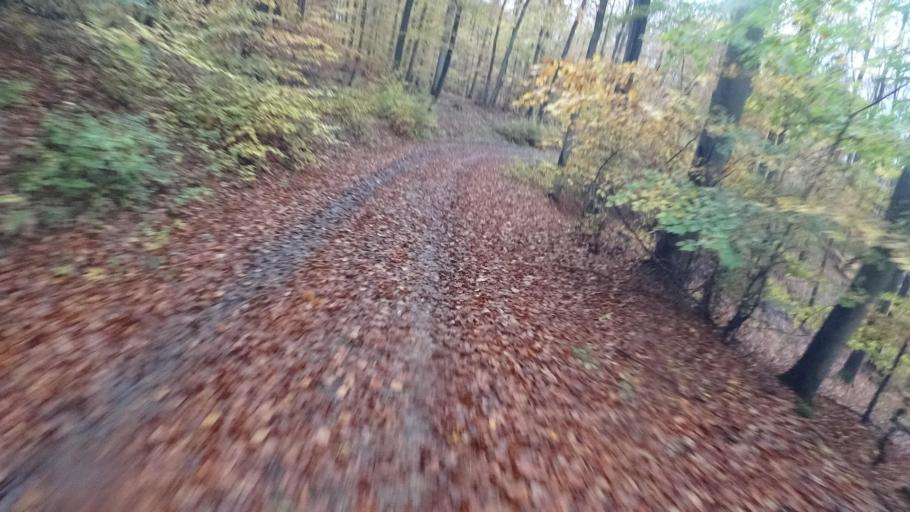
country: DE
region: Rheinland-Pfalz
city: Utzenhain
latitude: 50.1360
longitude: 7.6643
